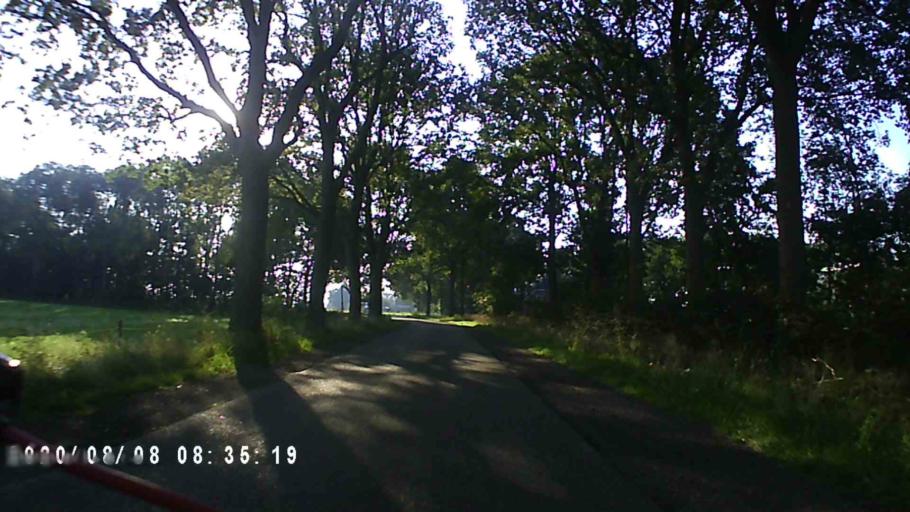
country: NL
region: Groningen
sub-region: Gemeente Leek
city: Leek
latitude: 53.0755
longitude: 6.3313
